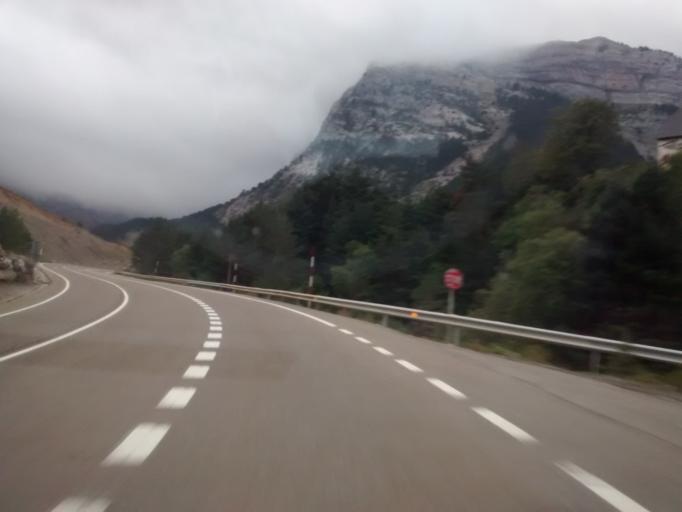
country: ES
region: Aragon
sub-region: Provincia de Huesca
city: Canfranc
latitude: 42.7759
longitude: -0.5124
